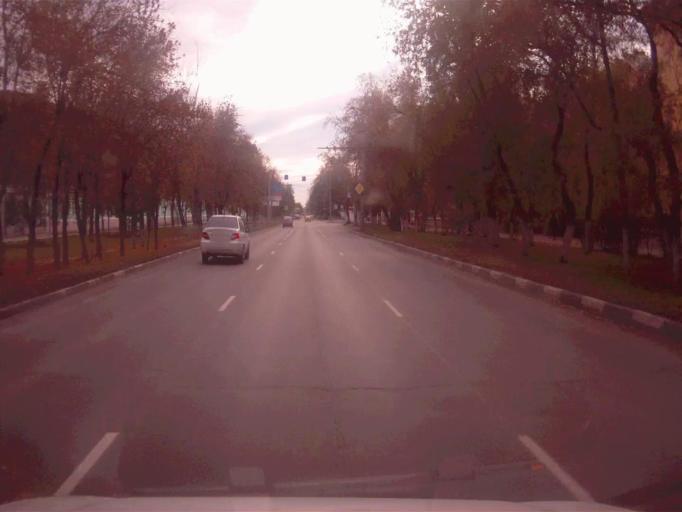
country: RU
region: Chelyabinsk
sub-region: Gorod Chelyabinsk
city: Chelyabinsk
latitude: 55.1223
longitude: 61.4734
